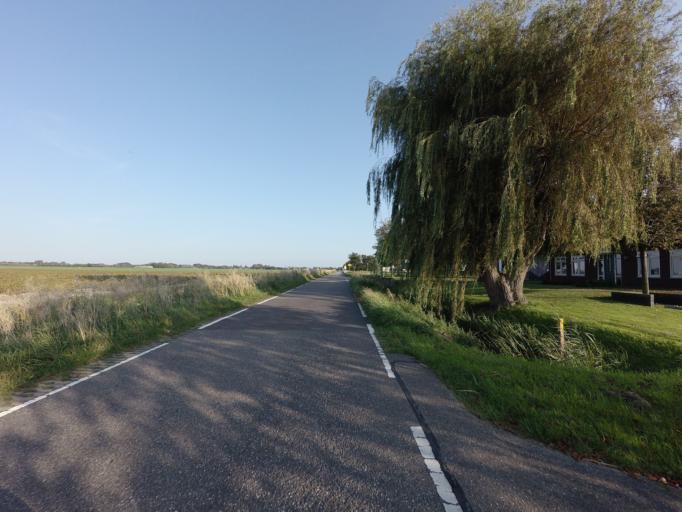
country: NL
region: South Holland
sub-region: Gemeente Waddinxveen
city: Groenswaard
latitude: 52.0434
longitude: 4.6104
